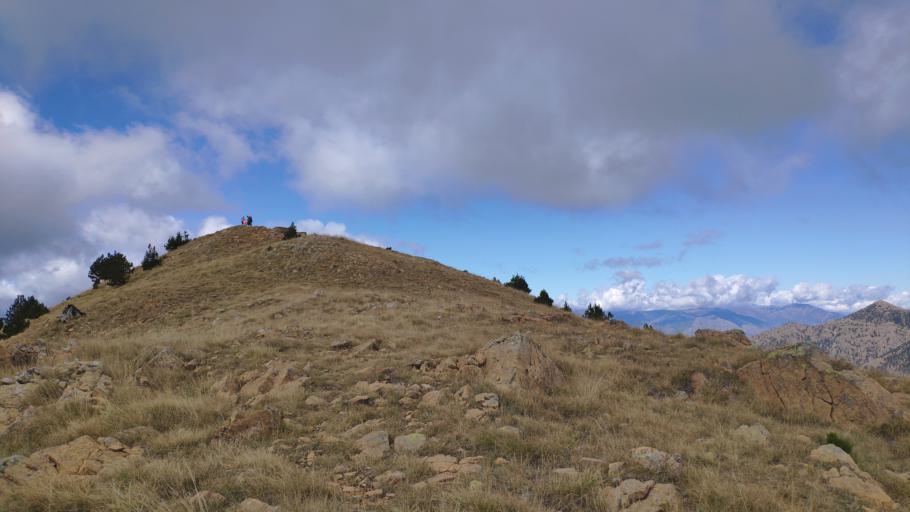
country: GR
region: Epirus
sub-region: Nomos Ioanninon
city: Metsovo
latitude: 39.8703
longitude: 21.1205
